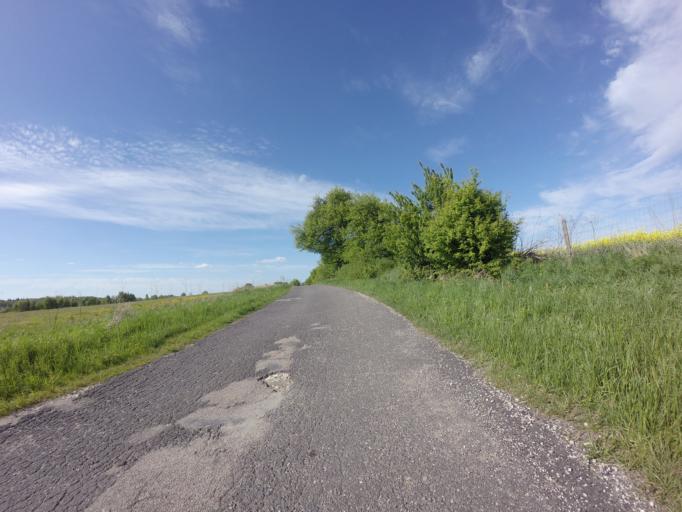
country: PL
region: West Pomeranian Voivodeship
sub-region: Powiat choszczenski
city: Drawno
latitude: 53.2055
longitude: 15.7638
